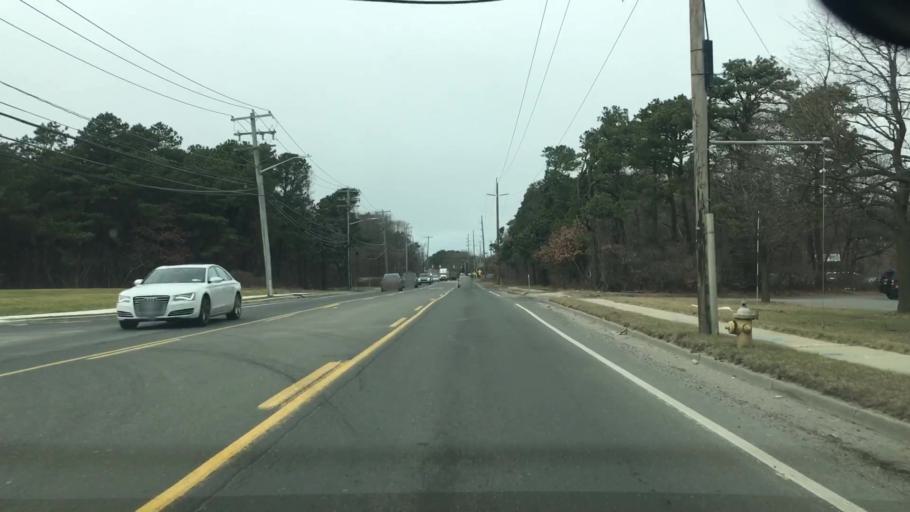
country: US
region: New York
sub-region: Suffolk County
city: Medford
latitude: 40.8169
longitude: -72.9622
